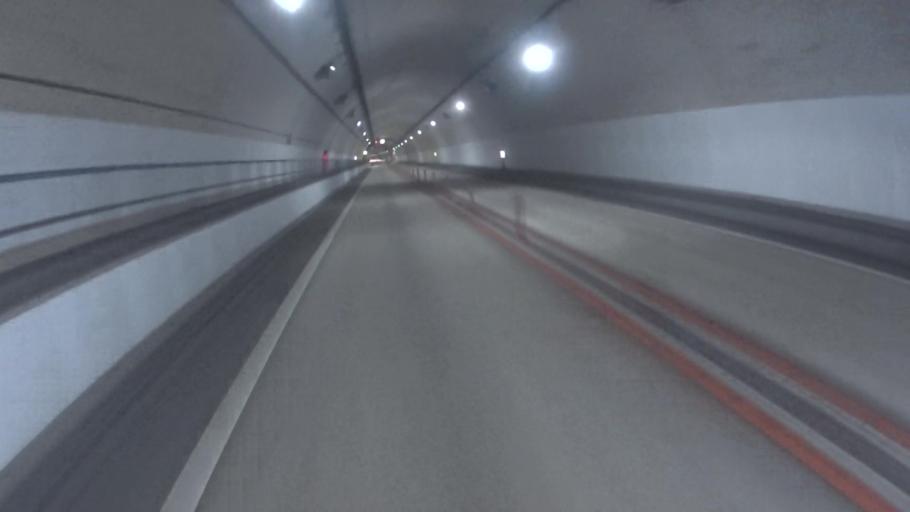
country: JP
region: Kyoto
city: Ayabe
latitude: 35.3037
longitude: 135.3293
